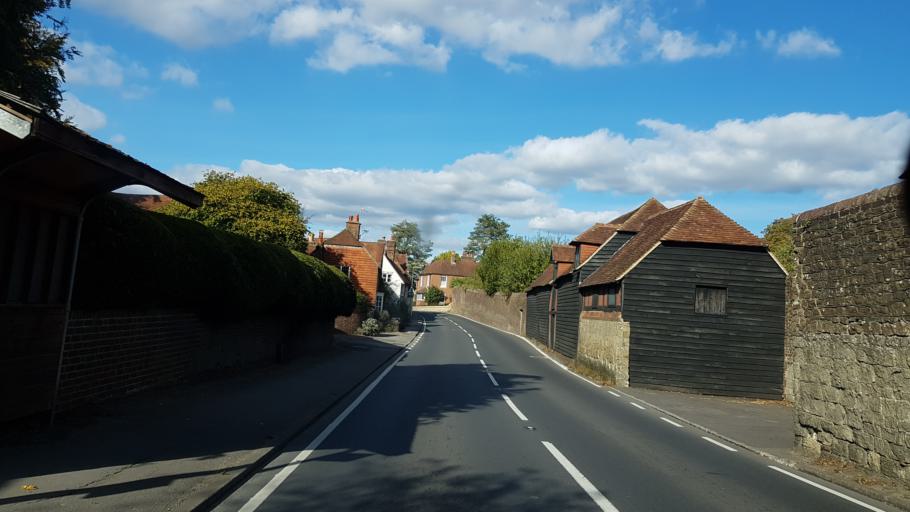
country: GB
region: England
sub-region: Surrey
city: Milford
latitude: 51.1489
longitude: -0.6468
